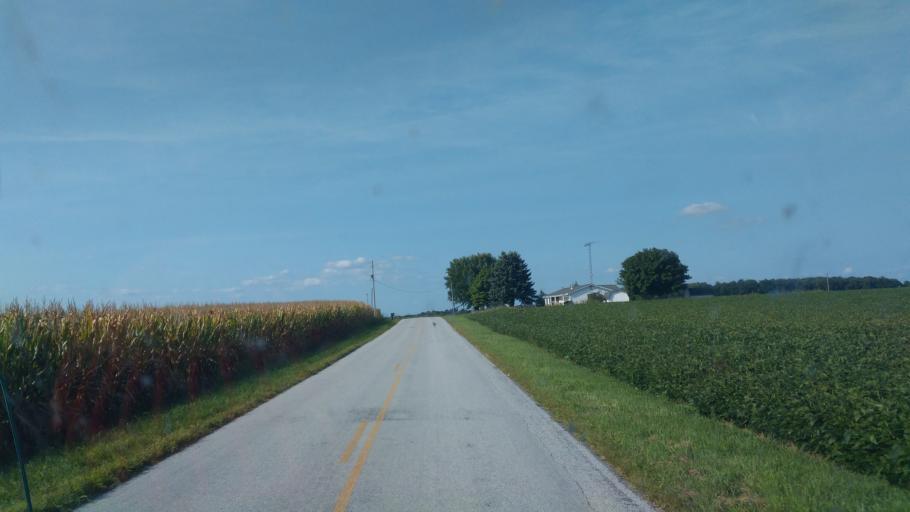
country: US
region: Ohio
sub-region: Hardin County
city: Kenton
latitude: 40.7222
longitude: -83.5725
